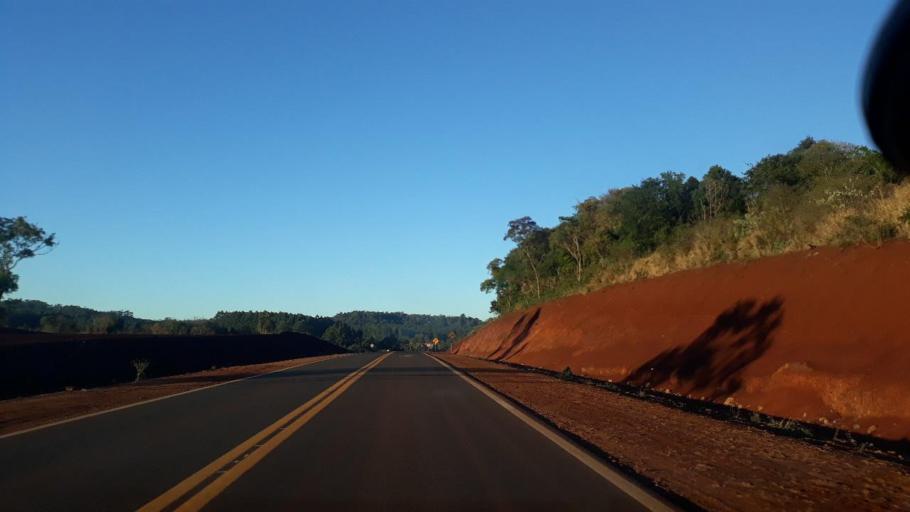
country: AR
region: Misiones
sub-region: Departamento de San Pedro
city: San Pedro
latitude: -26.5445
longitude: -53.9599
